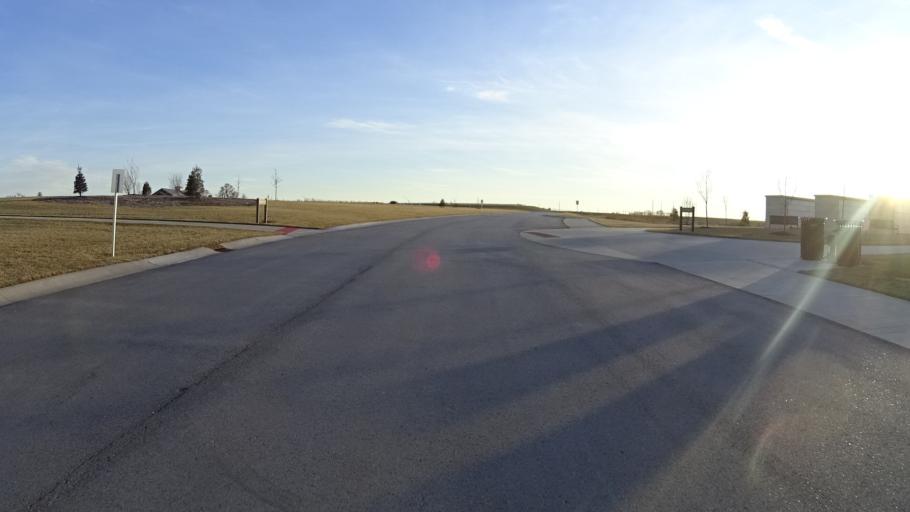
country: US
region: Nebraska
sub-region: Sarpy County
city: Chalco
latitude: 41.1373
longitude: -96.1339
